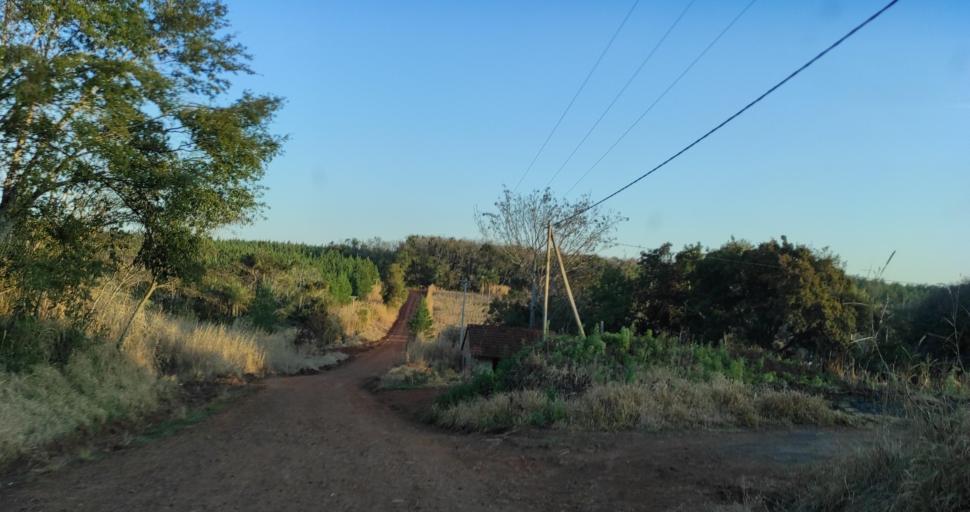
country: AR
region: Misiones
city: Capiovi
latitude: -26.8784
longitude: -55.1229
